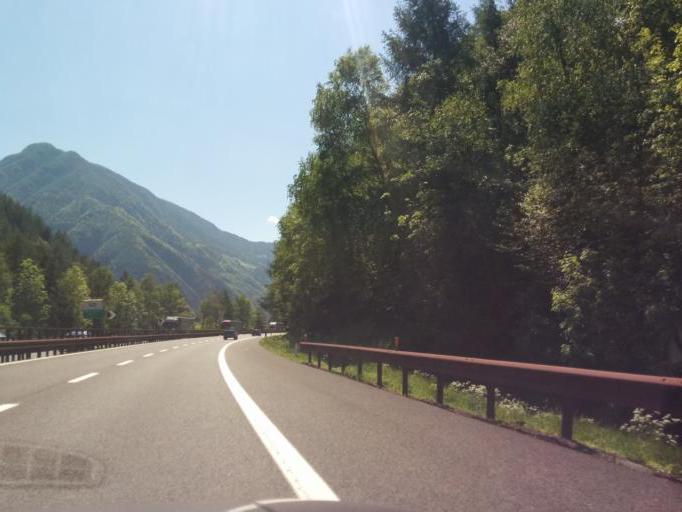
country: IT
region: Trentino-Alto Adige
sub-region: Bolzano
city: Campo di Trens
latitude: 46.8607
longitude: 11.5058
